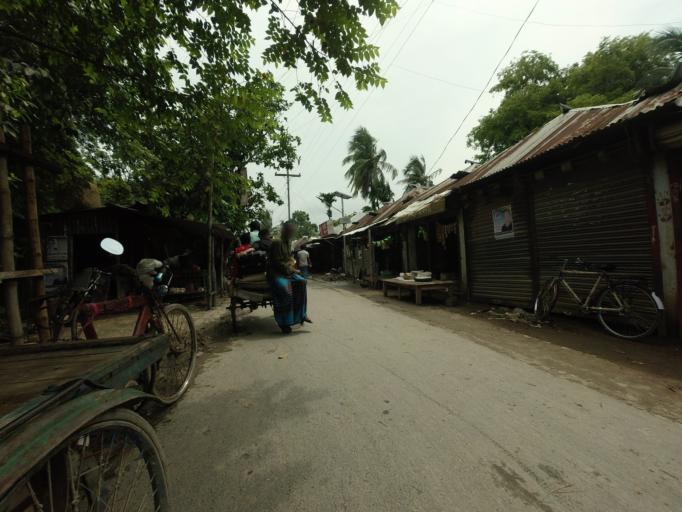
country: BD
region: Khulna
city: Kalia
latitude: 23.0849
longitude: 89.6708
